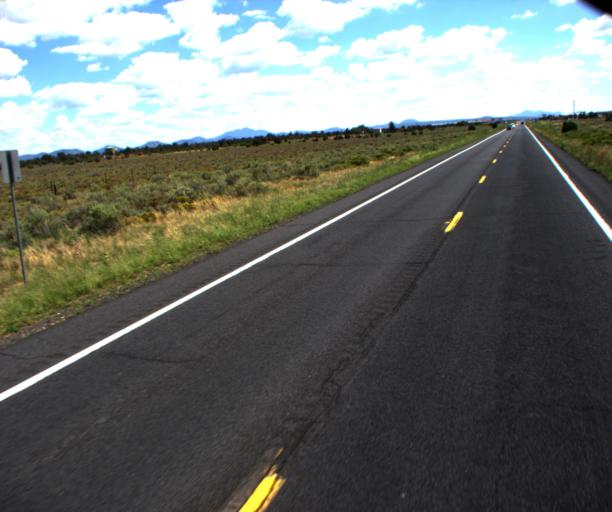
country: US
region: Arizona
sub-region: Coconino County
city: Grand Canyon Village
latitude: 35.6641
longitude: -112.1379
